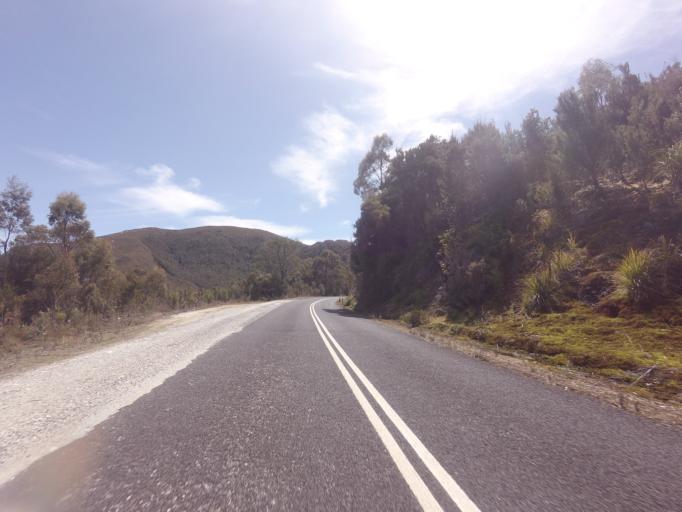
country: AU
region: Tasmania
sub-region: West Coast
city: Queenstown
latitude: -42.7968
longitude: 146.0873
